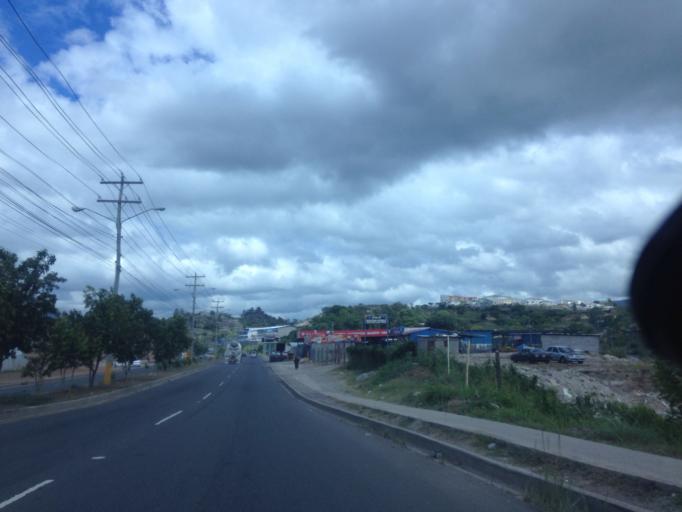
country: HN
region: Francisco Morazan
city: Yaguacire
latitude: 14.0437
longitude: -87.2392
